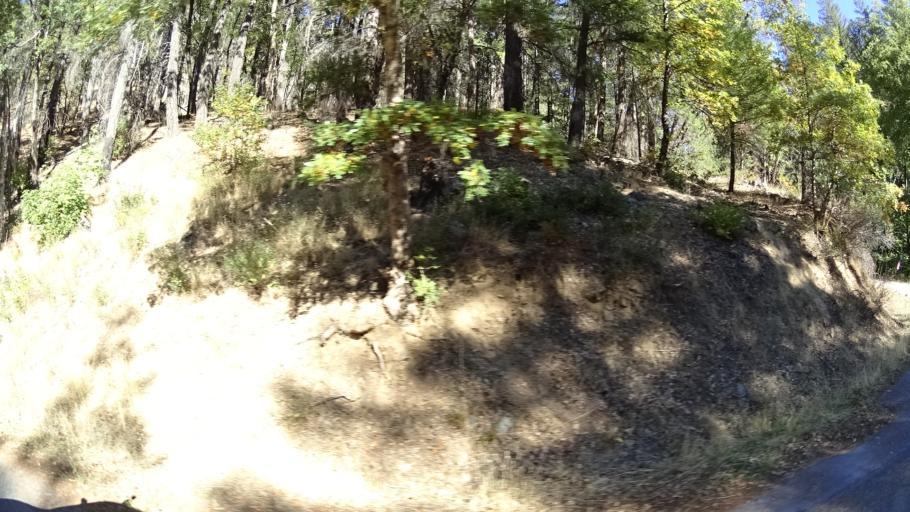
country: US
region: California
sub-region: Siskiyou County
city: Happy Camp
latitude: 41.3162
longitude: -123.1681
